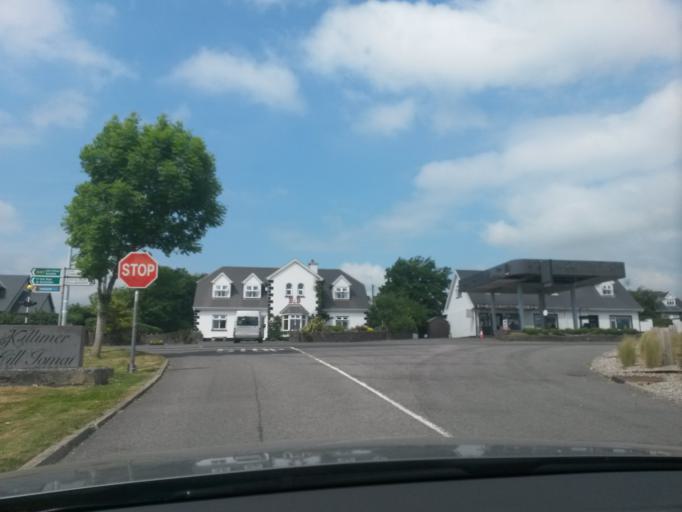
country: IE
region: Munster
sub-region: An Clar
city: Kilrush
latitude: 52.6170
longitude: -9.3819
